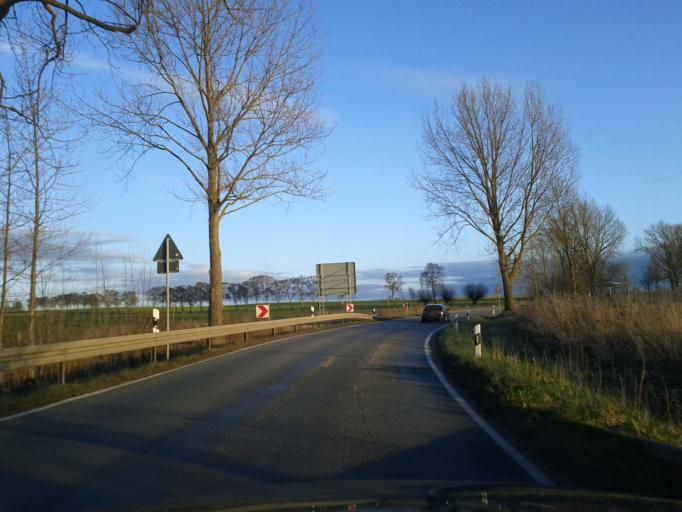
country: DE
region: Mecklenburg-Vorpommern
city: Blowatz
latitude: 53.9999
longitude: 11.4471
